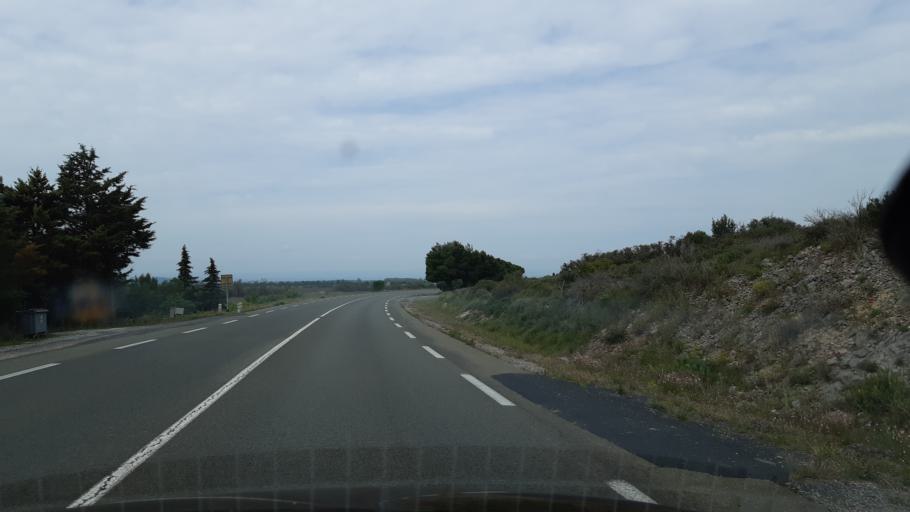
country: FR
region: Languedoc-Roussillon
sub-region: Departement de l'Aude
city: Gruissan
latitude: 43.1325
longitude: 3.0535
